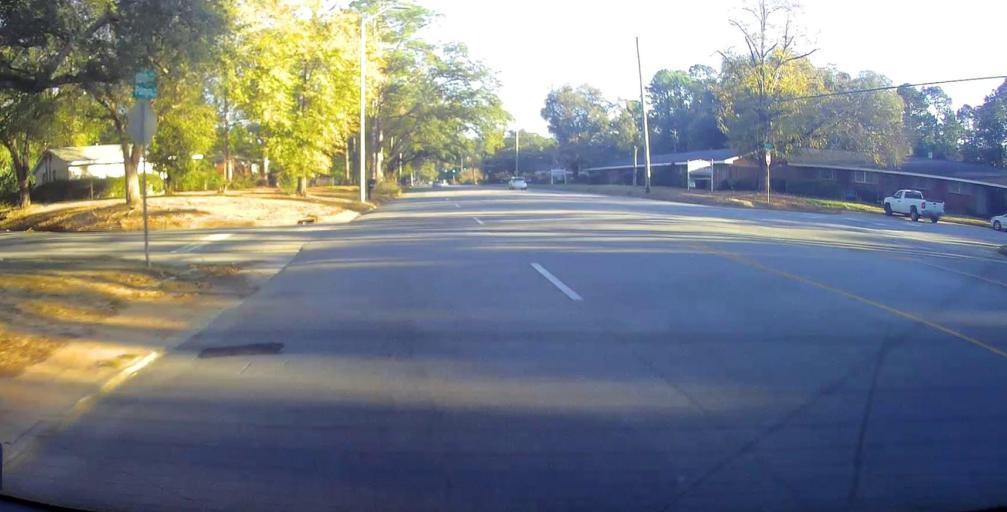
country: US
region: Georgia
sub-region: Dougherty County
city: Albany
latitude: 31.5988
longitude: -84.1651
